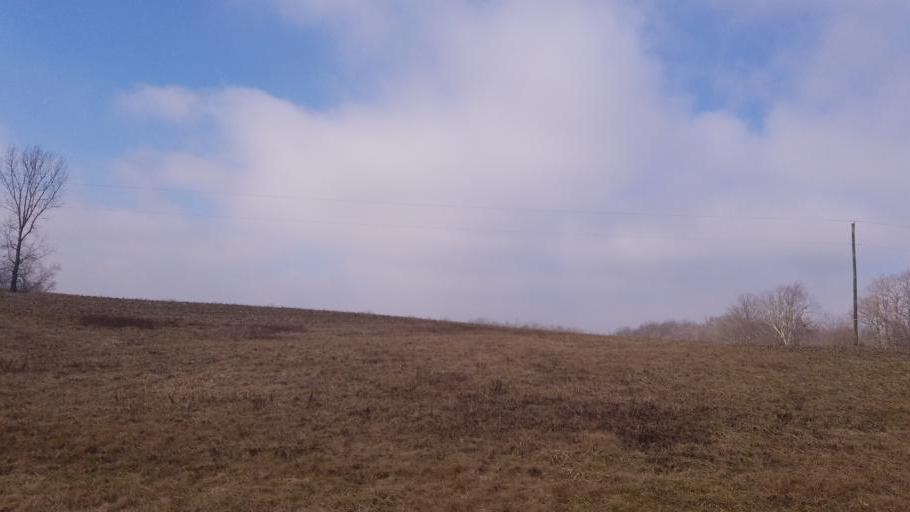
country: US
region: Ohio
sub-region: Crawford County
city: Galion
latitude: 40.6678
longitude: -82.8604
